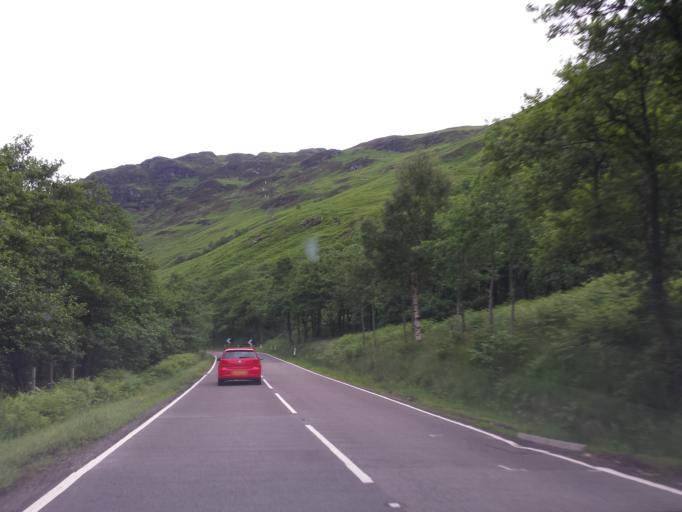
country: GB
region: Scotland
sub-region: Stirling
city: Callander
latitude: 56.4040
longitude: -4.3048
